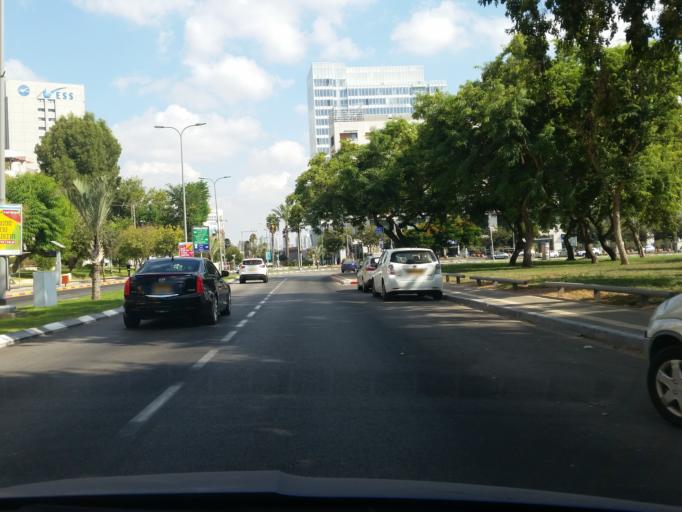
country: IL
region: Tel Aviv
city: Ramat HaSharon
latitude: 32.1153
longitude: 34.8396
